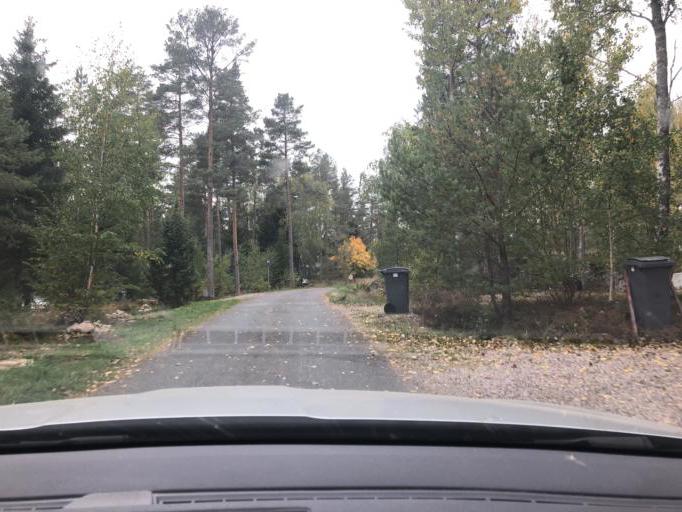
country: SE
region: Vaestmanland
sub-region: Kungsors Kommun
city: Kungsoer
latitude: 59.2282
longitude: 16.0826
